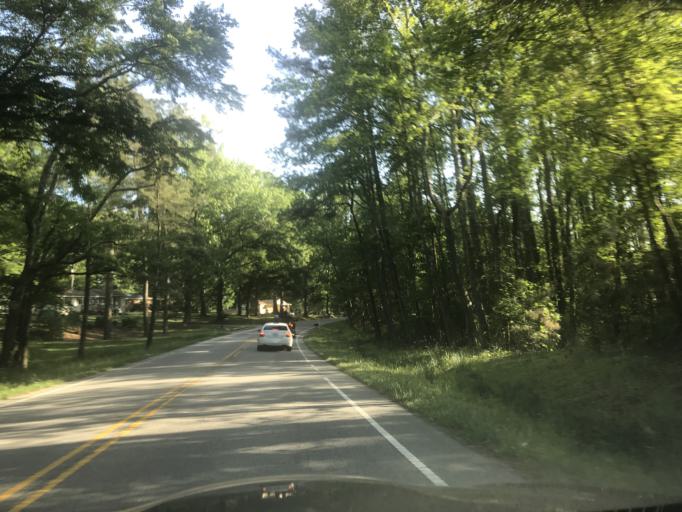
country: US
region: North Carolina
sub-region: Wake County
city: Knightdale
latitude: 35.7553
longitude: -78.4271
